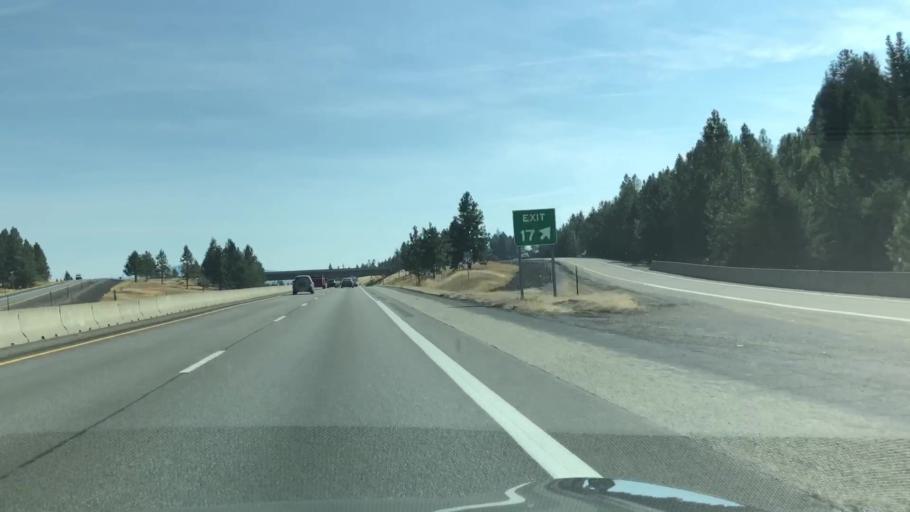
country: US
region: Idaho
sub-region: Kootenai County
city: Coeur d'Alene
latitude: 47.6583
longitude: -116.7280
